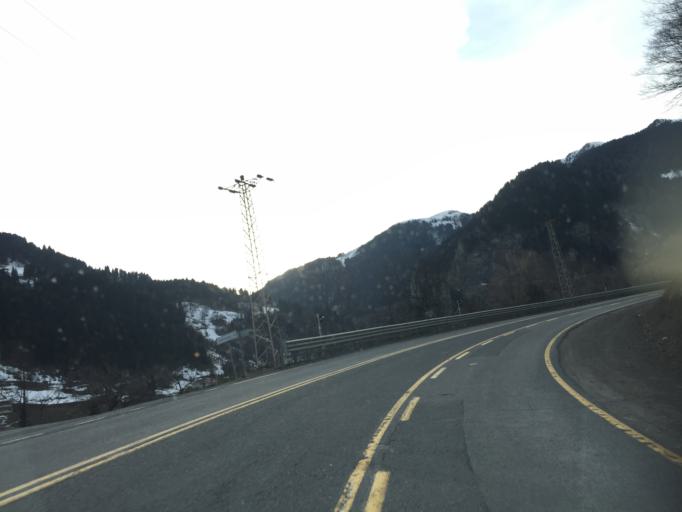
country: TR
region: Gumushane
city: Yaglidere
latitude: 40.6985
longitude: 39.4772
